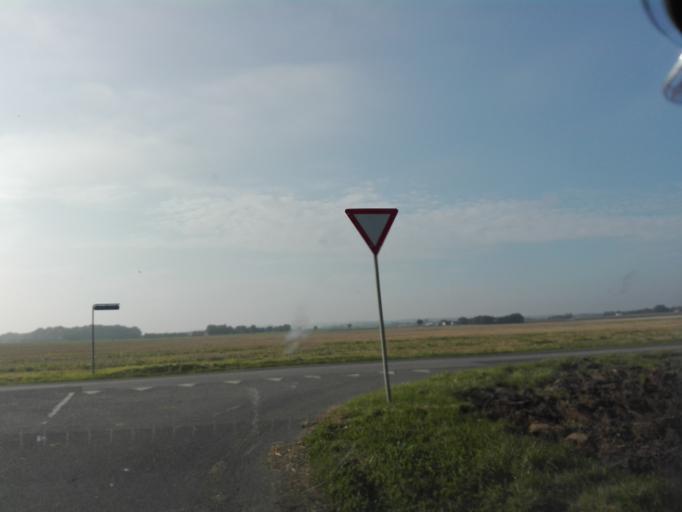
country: DK
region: Central Jutland
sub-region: Odder Kommune
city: Odder
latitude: 55.8790
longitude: 10.1706
